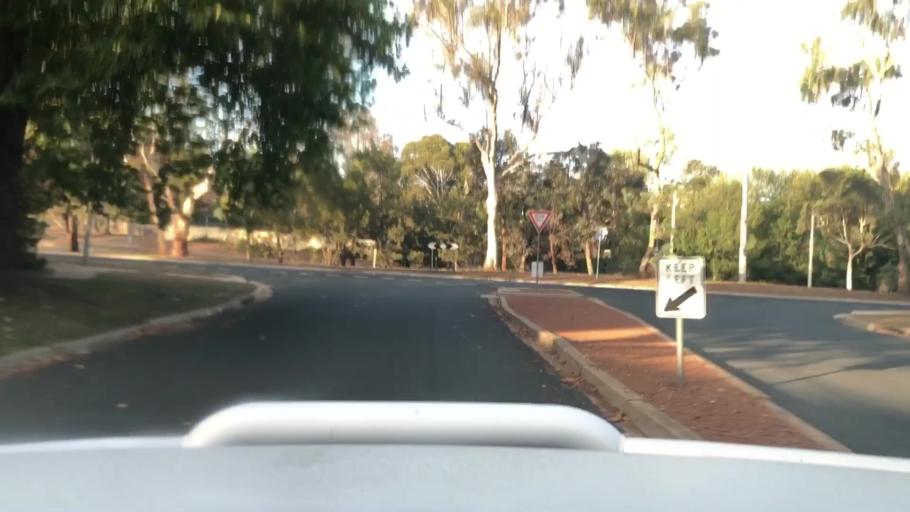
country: AU
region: Australian Capital Territory
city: Canberra
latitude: -35.2531
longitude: 149.1603
